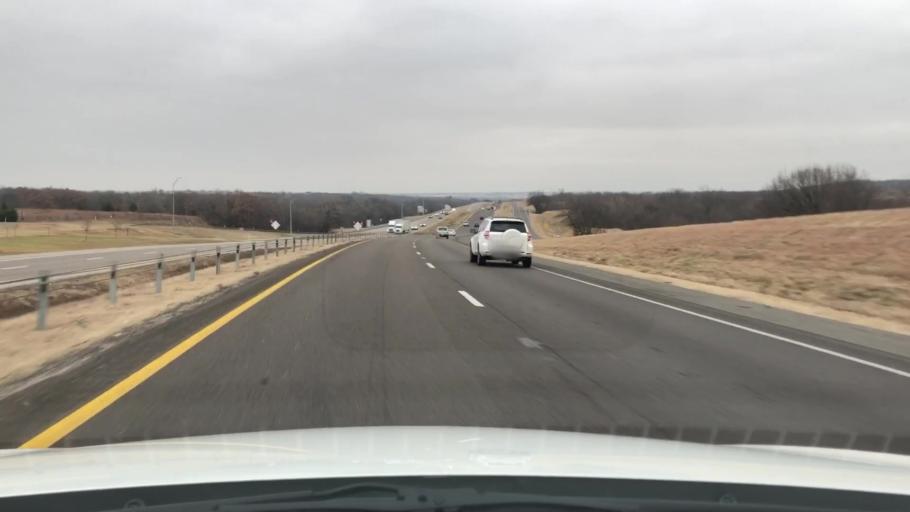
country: US
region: Texas
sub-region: Cooke County
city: Gainesville
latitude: 33.6930
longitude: -97.1622
